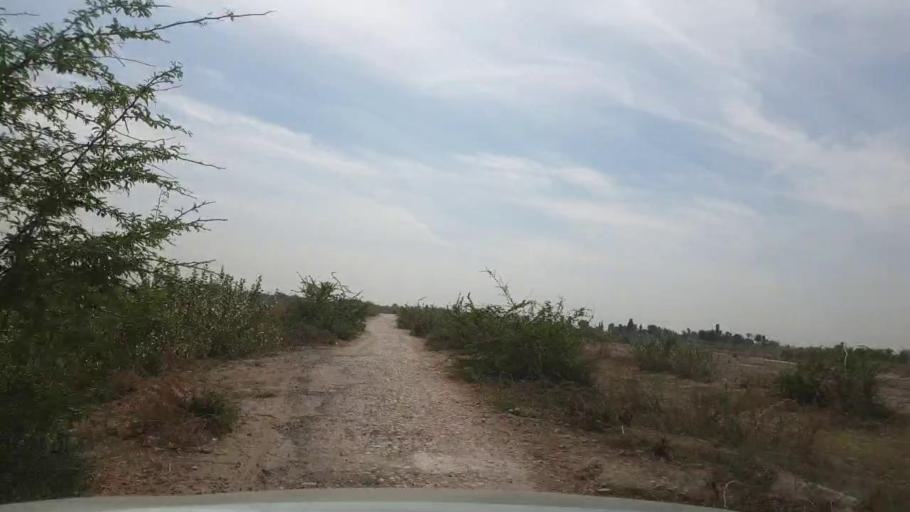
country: PK
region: Sindh
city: Nabisar
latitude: 25.0773
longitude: 69.5989
